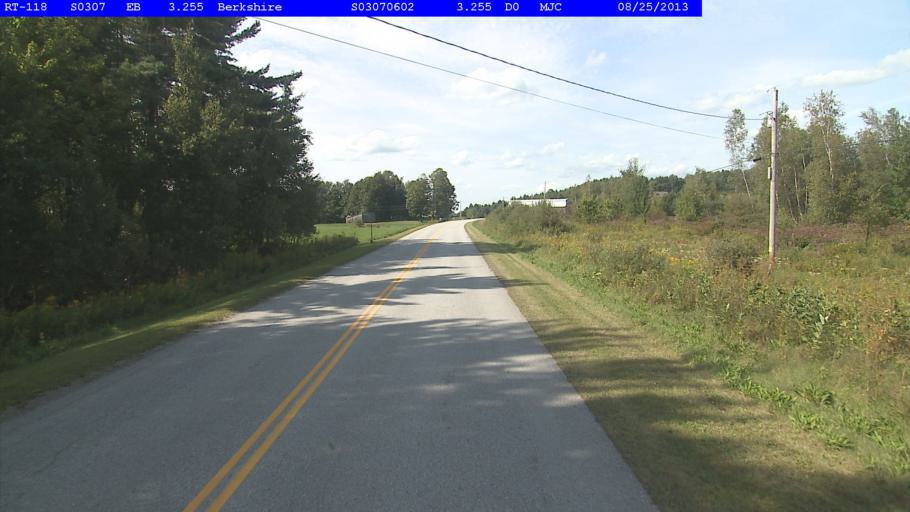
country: US
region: Vermont
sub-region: Franklin County
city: Enosburg Falls
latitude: 44.9624
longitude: -72.7584
